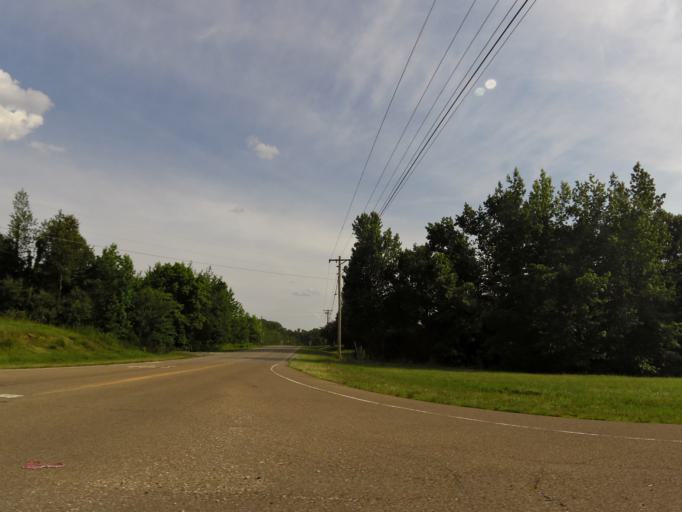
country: US
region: Tennessee
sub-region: Benton County
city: Camden
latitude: 36.0339
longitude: -88.1129
